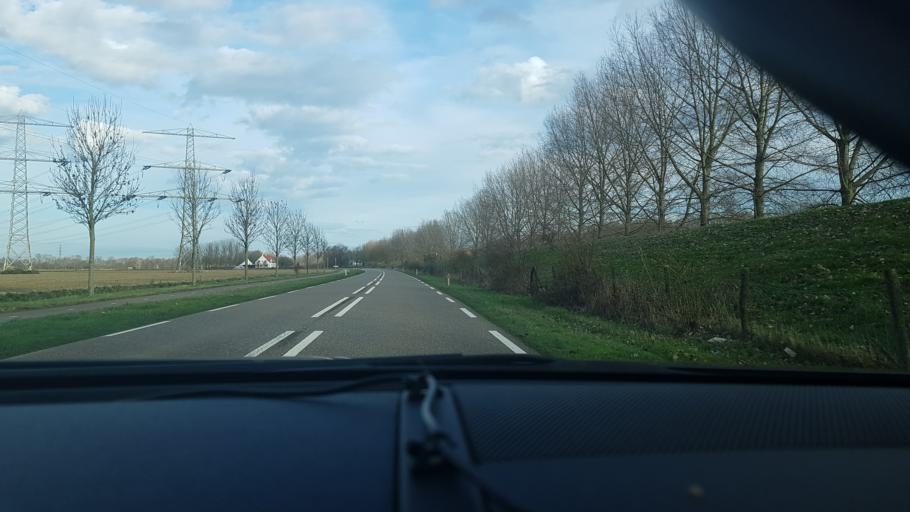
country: NL
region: Limburg
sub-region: Gemeente Leudal
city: Haelen
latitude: 51.2088
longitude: 5.9633
